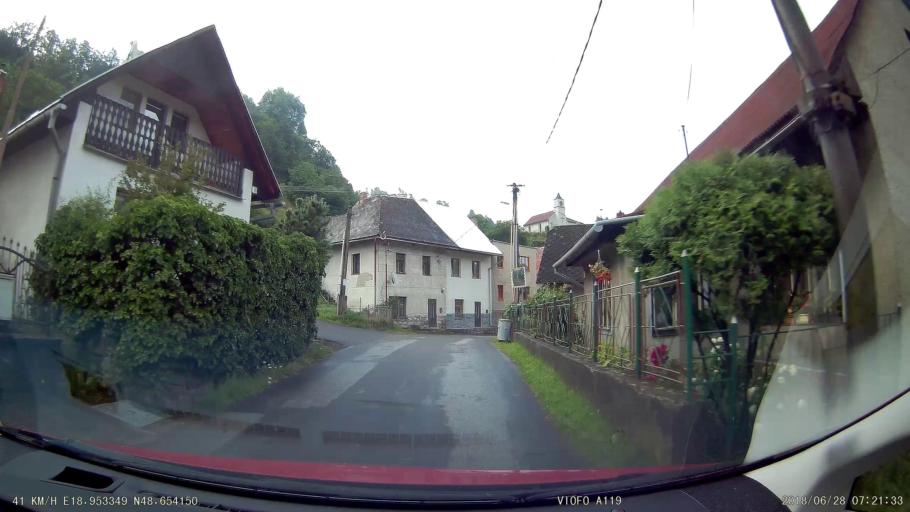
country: SK
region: Banskobystricky
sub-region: Okres Ziar nad Hronom
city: Kremnica
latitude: 48.6540
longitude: 18.9535
